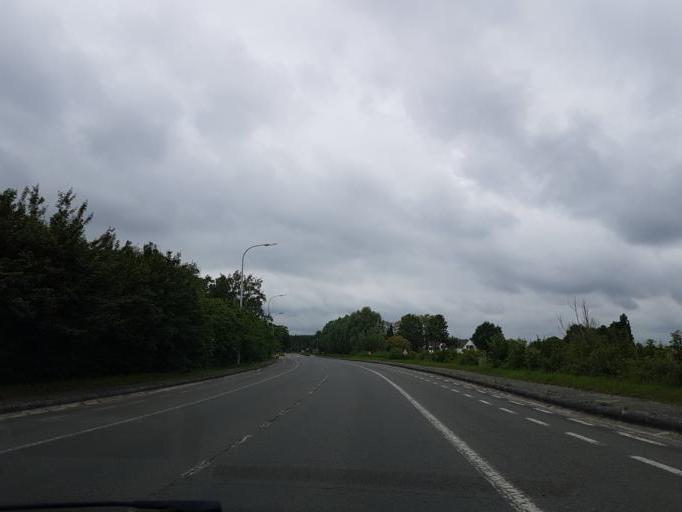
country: BE
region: Flanders
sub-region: Provincie Oost-Vlaanderen
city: Zomergem
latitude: 51.0968
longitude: 3.5732
